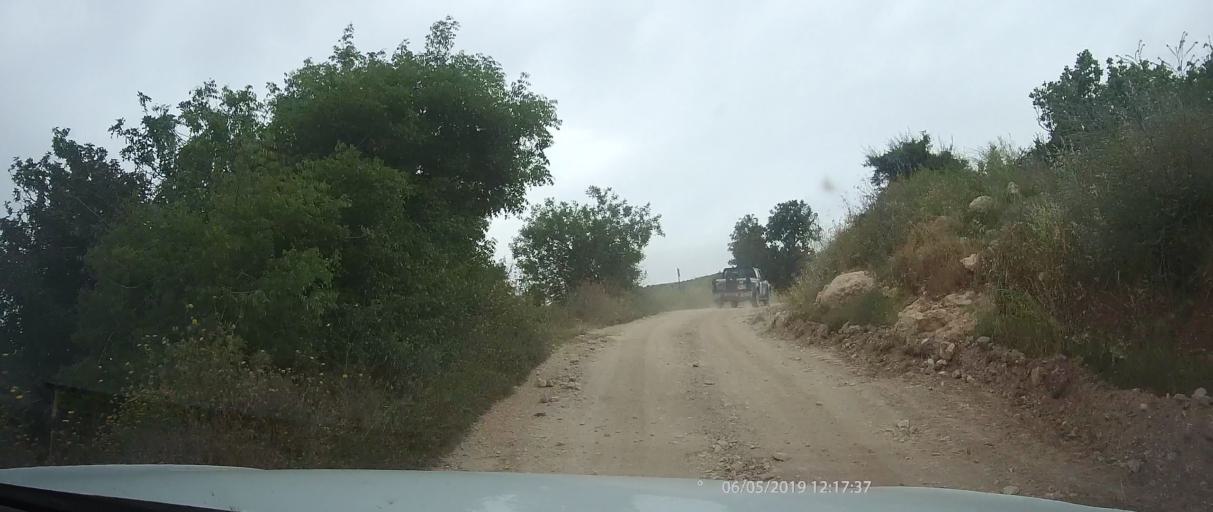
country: CY
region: Pafos
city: Tala
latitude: 34.8579
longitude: 32.4242
